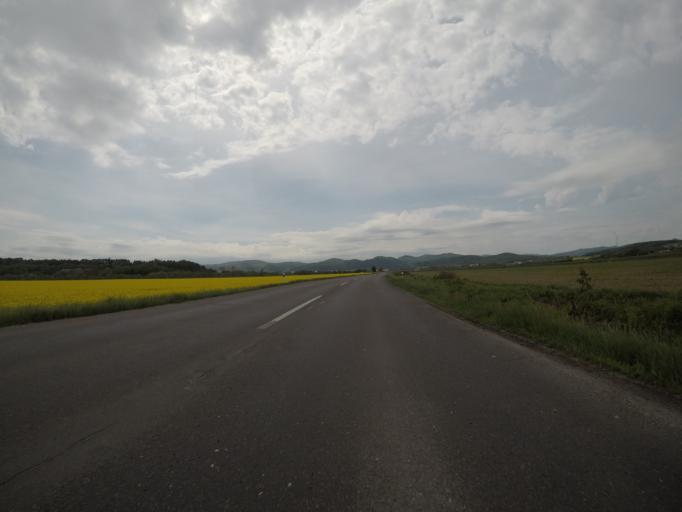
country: SK
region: Banskobystricky
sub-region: Okres Banska Bystrica
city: Zvolen
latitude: 48.6061
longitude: 19.1263
